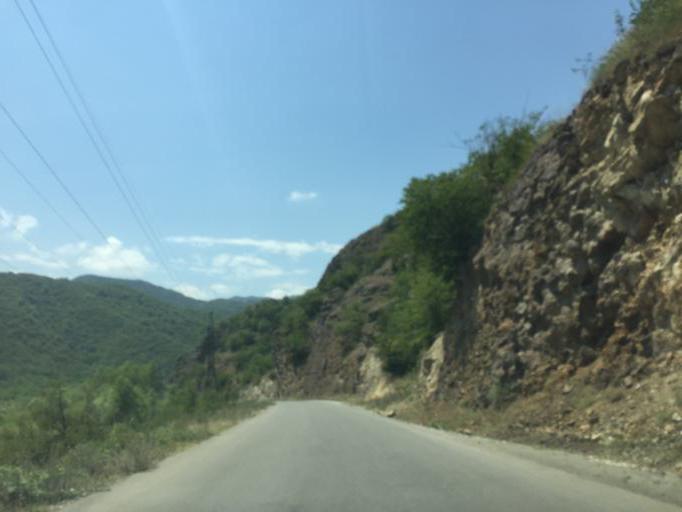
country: AZ
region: Kalbacar Rayonu
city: Kerbakhiar
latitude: 40.1351
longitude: 46.3760
